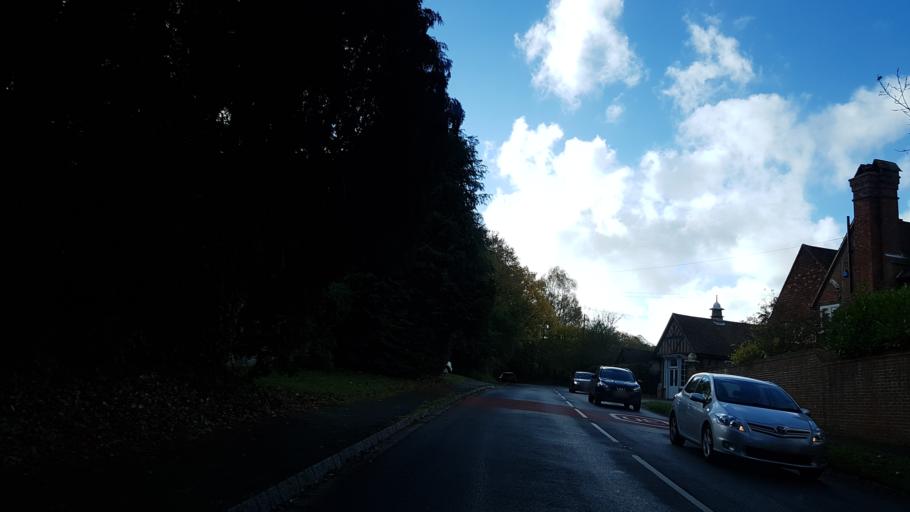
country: GB
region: England
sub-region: Surrey
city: Milford
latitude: 51.1338
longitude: -0.6721
